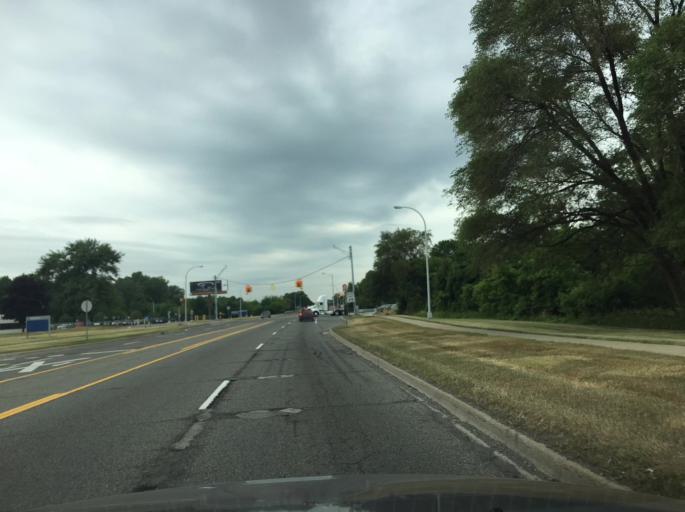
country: US
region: Michigan
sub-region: Macomb County
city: Center Line
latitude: 42.5061
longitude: -83.0392
